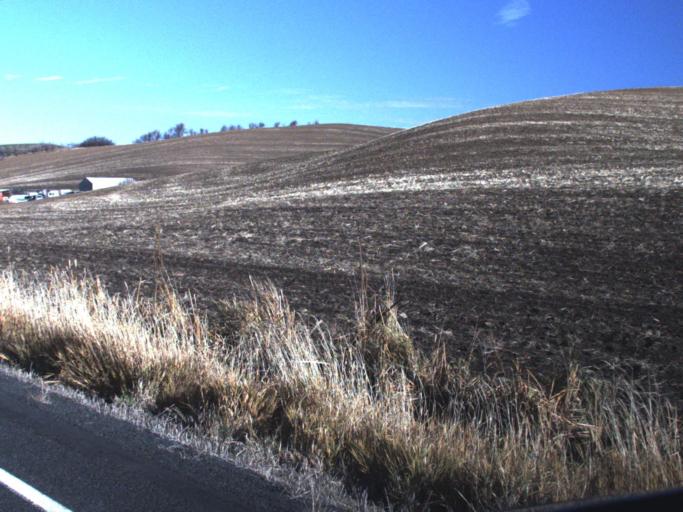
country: US
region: Washington
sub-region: Whitman County
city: Colfax
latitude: 46.7549
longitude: -117.3777
